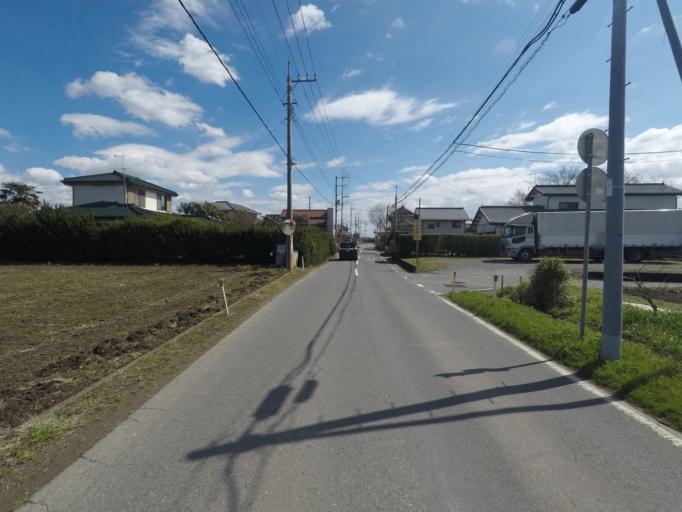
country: JP
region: Ibaraki
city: Fujishiro
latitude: 35.9427
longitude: 140.0913
